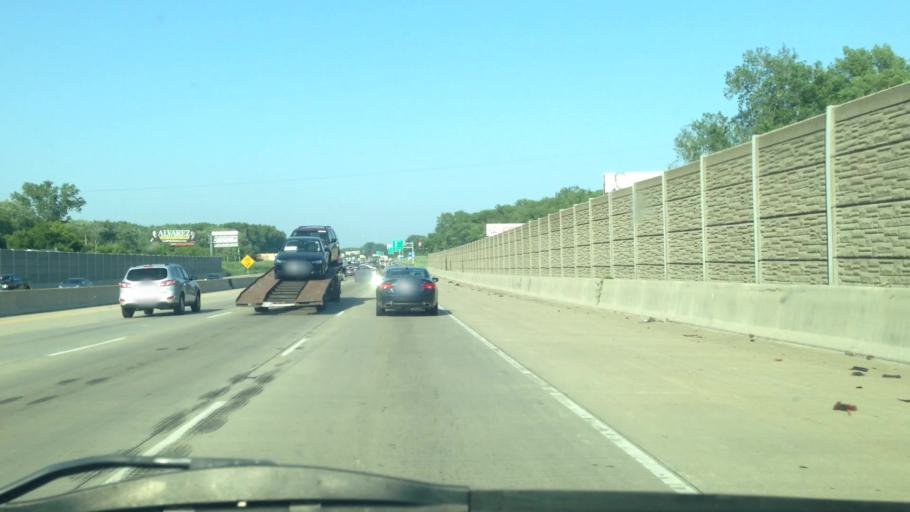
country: US
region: Indiana
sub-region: Lake County
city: New Chicago
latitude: 41.5730
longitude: -87.2750
